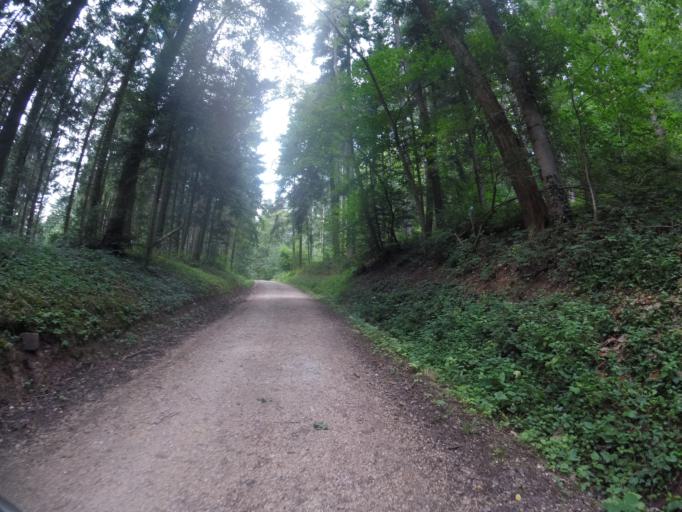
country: DE
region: Baden-Wuerttemberg
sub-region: Regierungsbezirk Stuttgart
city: Mutlangen
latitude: 48.8149
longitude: 9.7951
